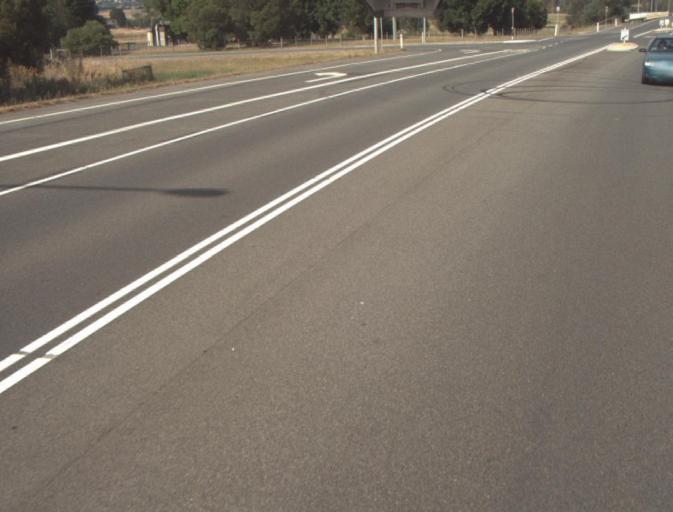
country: AU
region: Tasmania
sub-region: Launceston
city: Newstead
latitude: -41.4614
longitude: 147.1925
